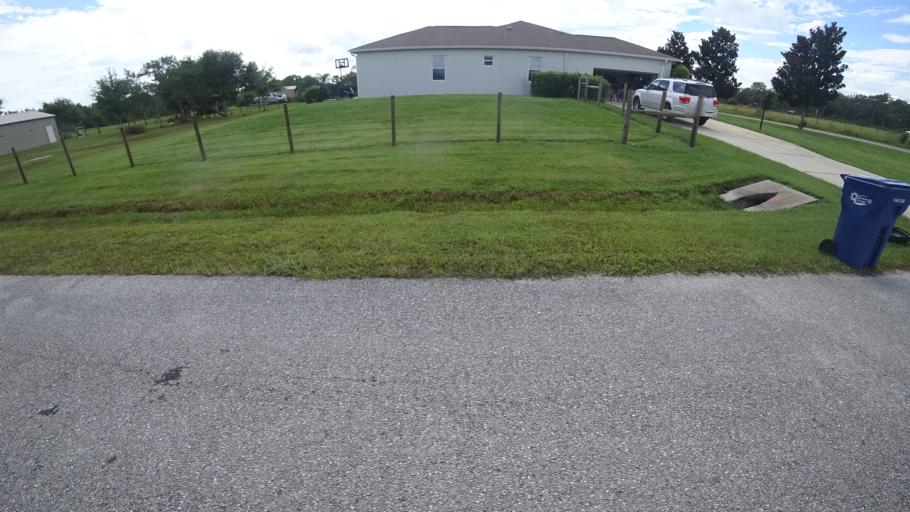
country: US
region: Florida
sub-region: Sarasota County
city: Lake Sarasota
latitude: 27.3886
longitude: -82.2753
